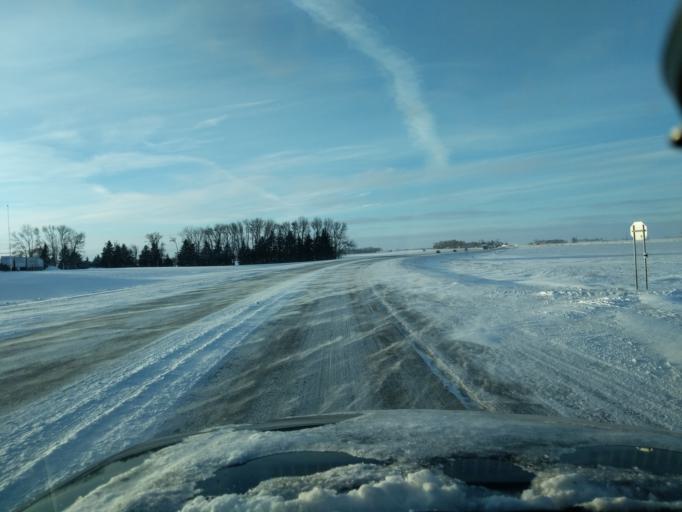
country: US
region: Minnesota
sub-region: Renville County
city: Bird Island
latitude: 44.7681
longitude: -94.9359
